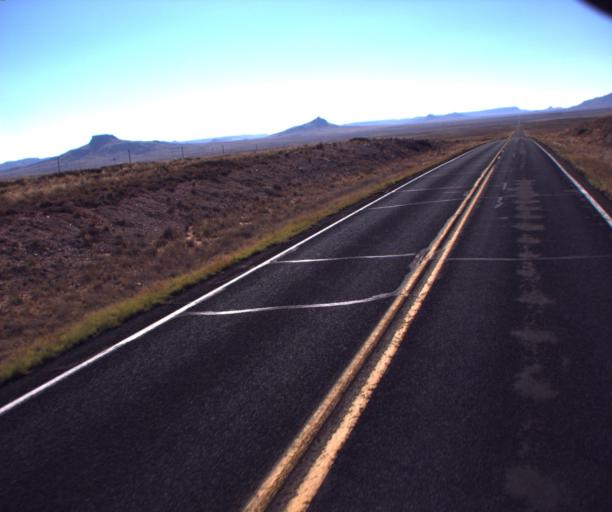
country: US
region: Arizona
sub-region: Navajo County
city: First Mesa
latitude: 35.6185
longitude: -110.4776
